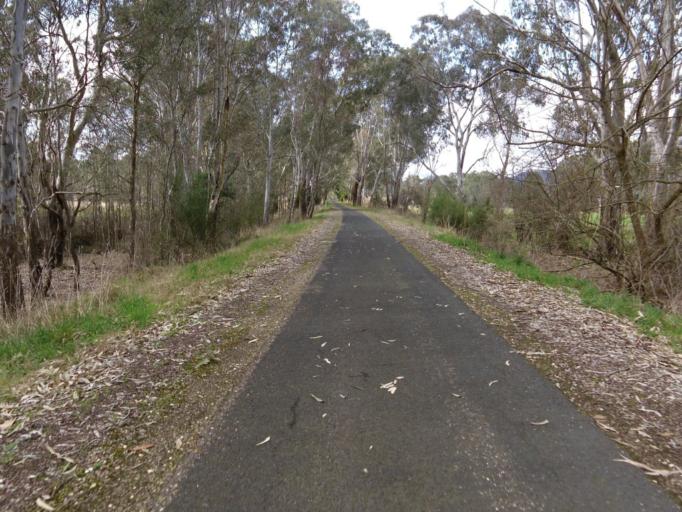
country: AU
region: Victoria
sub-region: Alpine
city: Mount Beauty
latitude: -36.5829
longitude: 146.7521
